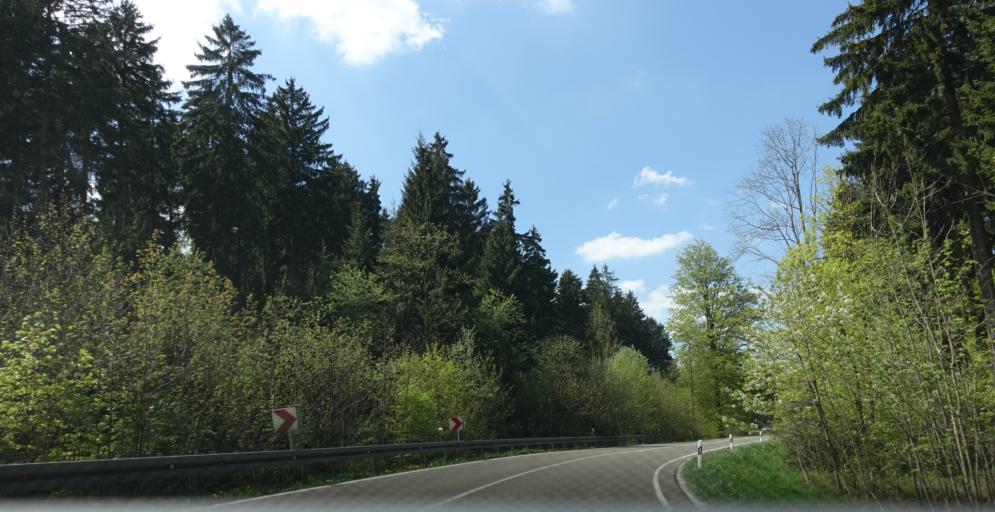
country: DE
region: Saxony
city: Lengefeld
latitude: 50.7015
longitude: 13.1671
